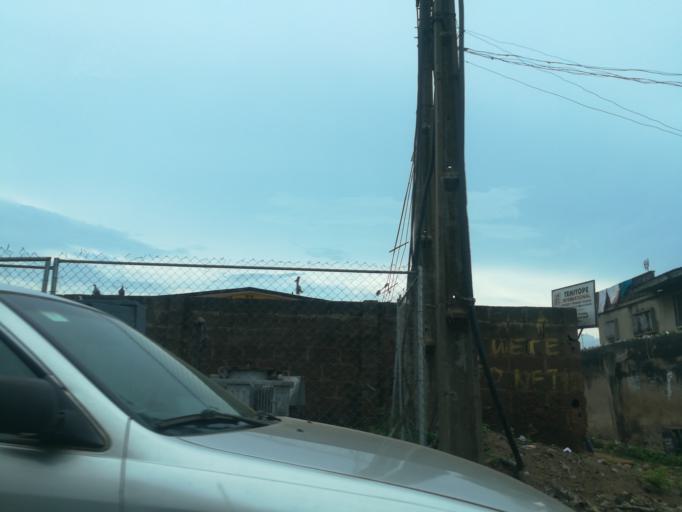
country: NG
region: Oyo
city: Ibadan
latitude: 7.4421
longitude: 3.9109
